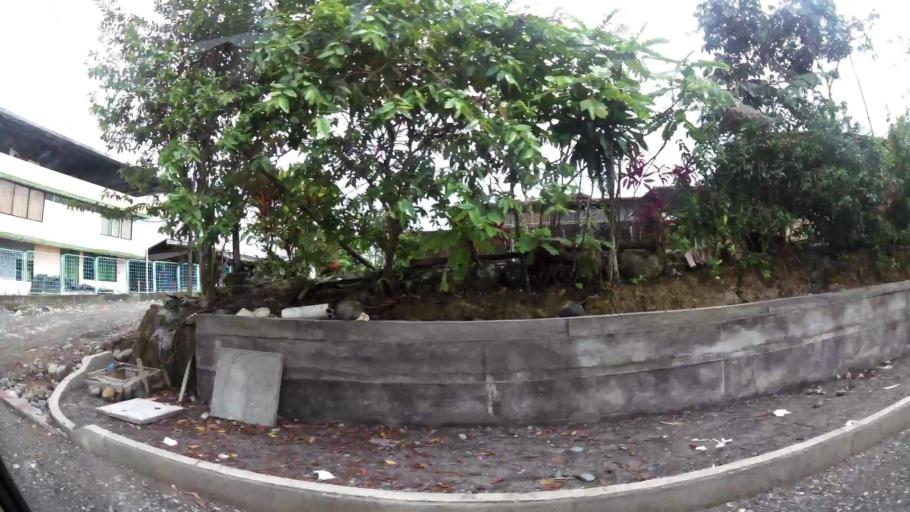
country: EC
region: Pastaza
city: Puyo
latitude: -1.4976
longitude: -77.9967
